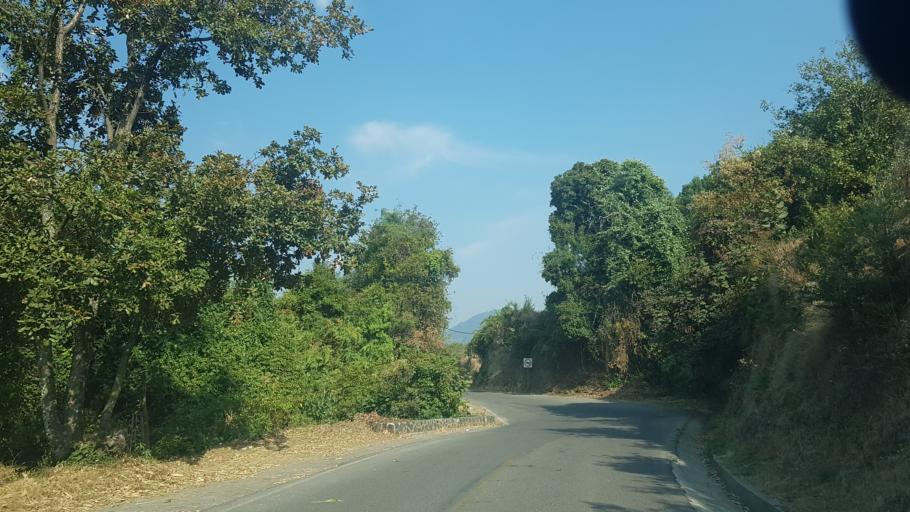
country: MX
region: Puebla
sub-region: Tochimilco
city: Santa Cruz Cuautomatitla
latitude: 18.8889
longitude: -98.6677
